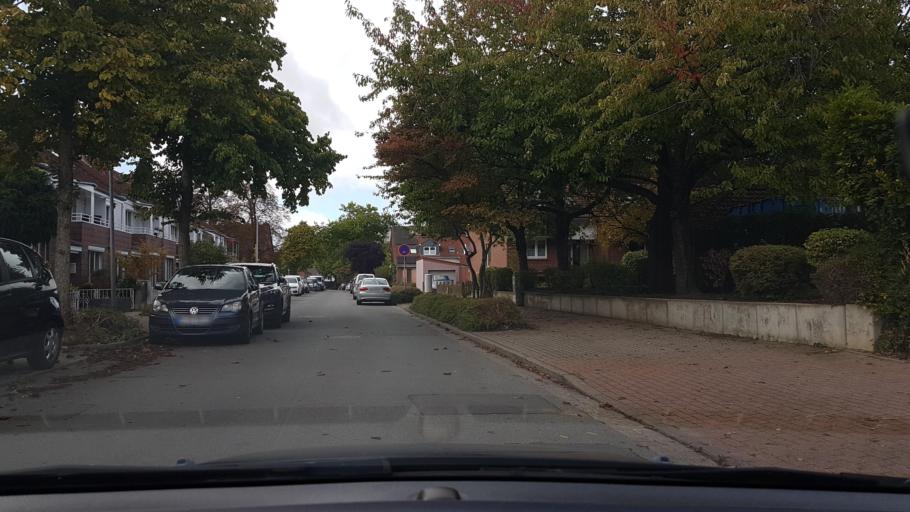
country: DE
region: Lower Saxony
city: Ronnenberg
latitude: 52.3419
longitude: 9.6759
